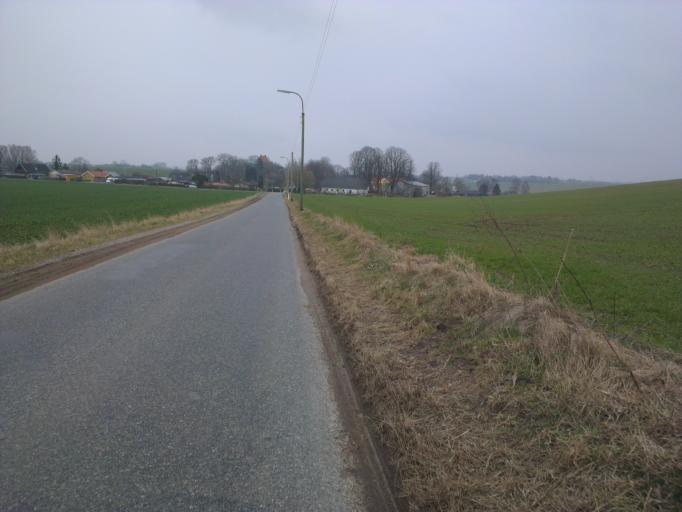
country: DK
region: Capital Region
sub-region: Egedal Kommune
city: Olstykke
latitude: 55.8017
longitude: 12.1210
